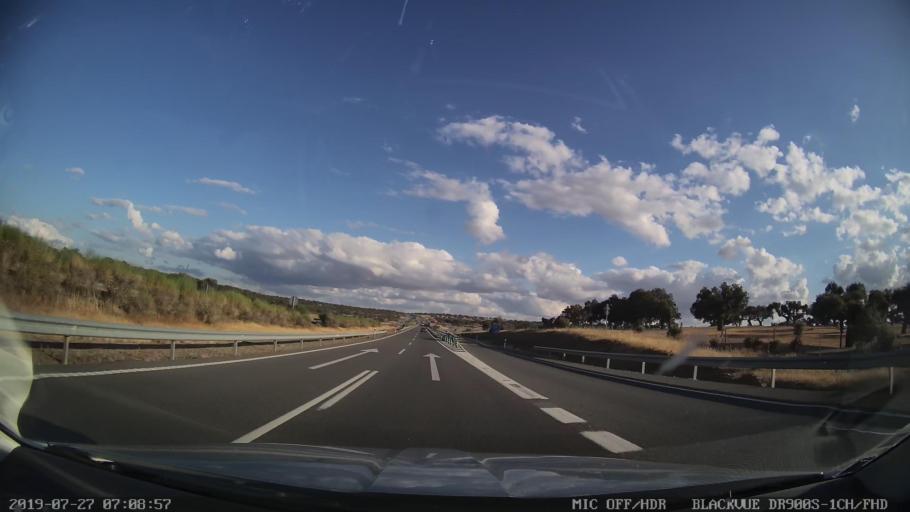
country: ES
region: Extremadura
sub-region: Provincia de Caceres
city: Jaraicejo
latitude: 39.6036
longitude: -5.8394
